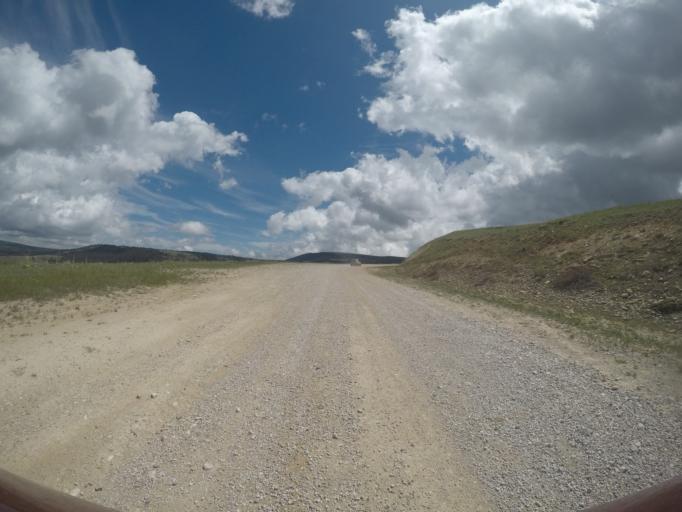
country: US
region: Wyoming
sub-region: Big Horn County
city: Lovell
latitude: 45.1896
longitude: -108.4746
